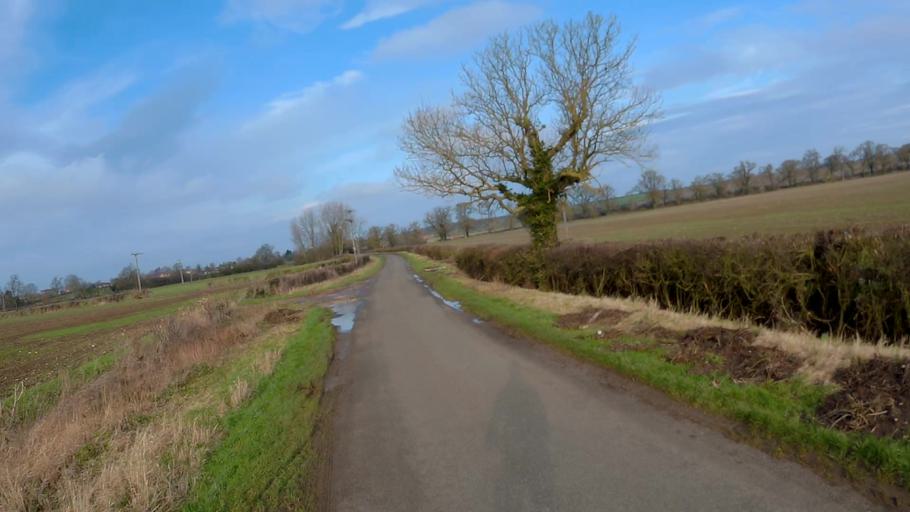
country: GB
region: England
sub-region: Lincolnshire
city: Bourne
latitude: 52.7739
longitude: -0.4259
